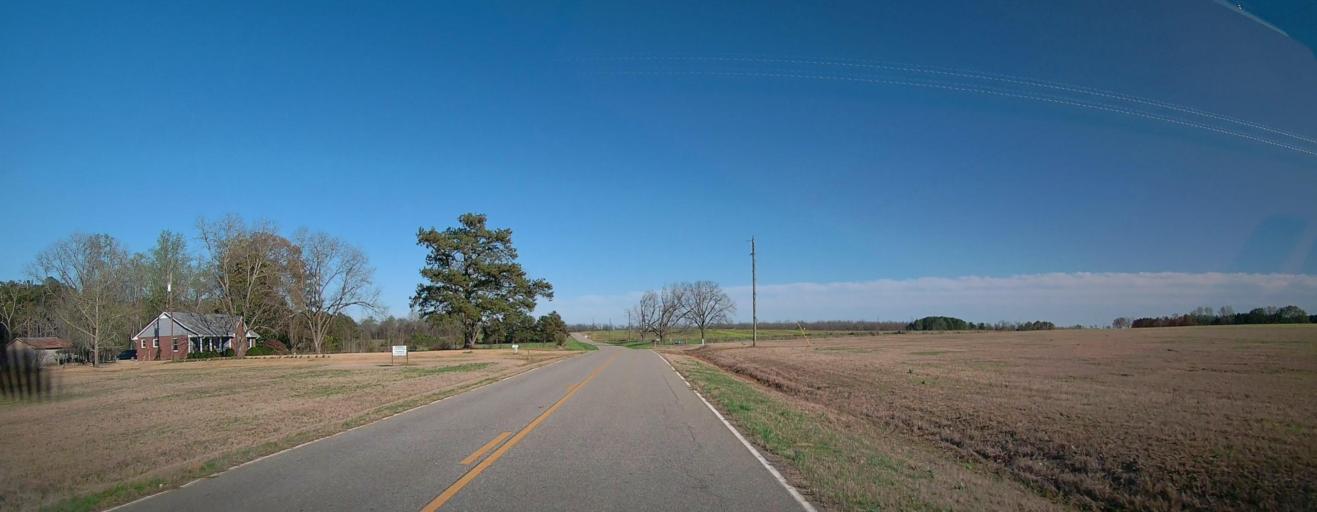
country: US
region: Georgia
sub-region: Houston County
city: Perry
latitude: 32.3696
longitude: -83.7009
